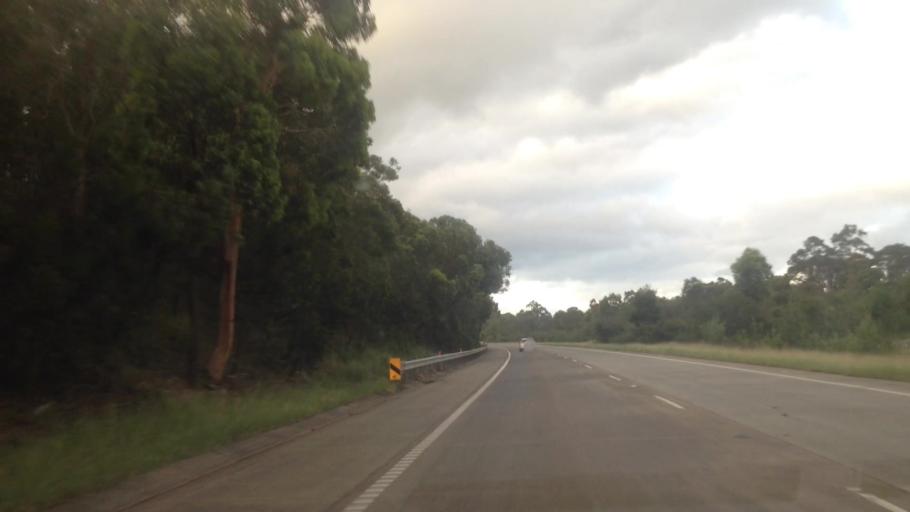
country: AU
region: New South Wales
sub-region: Wyong Shire
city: Charmhaven
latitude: -33.1935
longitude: 151.4662
